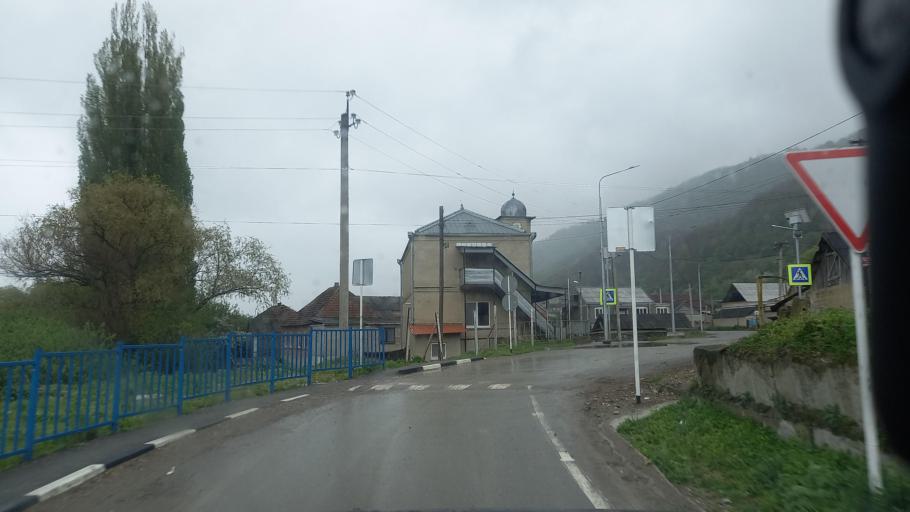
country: RU
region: Kabardino-Balkariya
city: Gundelen
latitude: 43.5965
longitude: 43.1530
